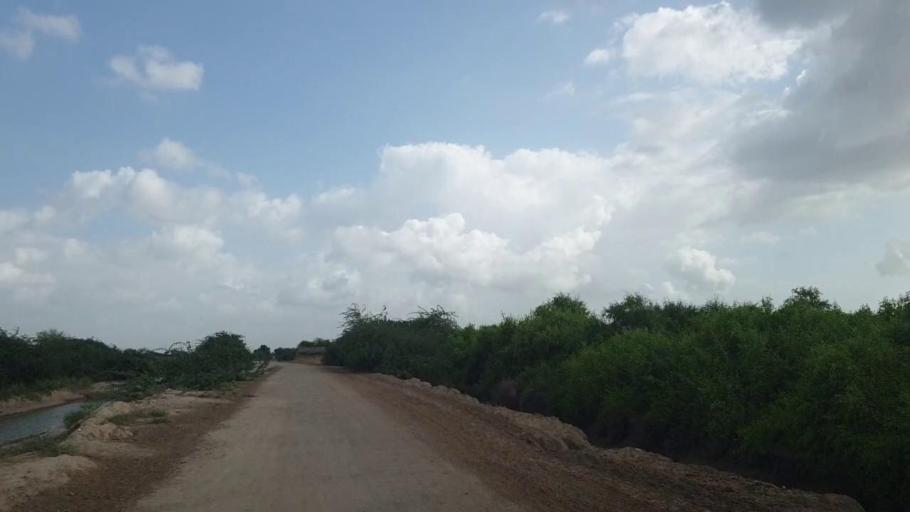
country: PK
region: Sindh
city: Kadhan
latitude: 24.5512
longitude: 69.0634
